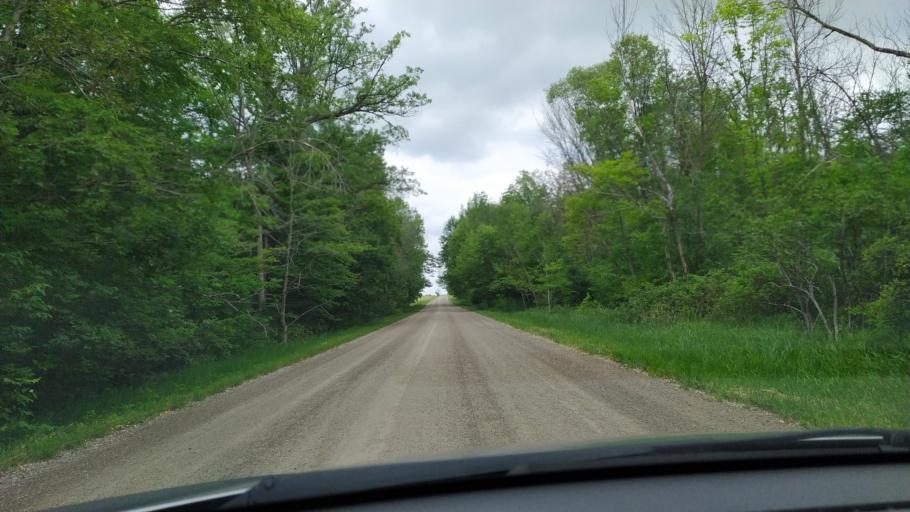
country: CA
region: Ontario
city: Stratford
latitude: 43.4173
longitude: -80.8882
